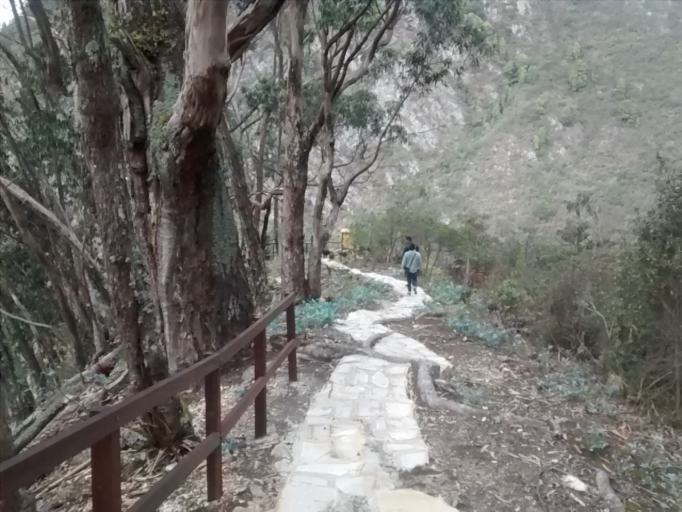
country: CO
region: Bogota D.C.
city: Bogota
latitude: 4.5984
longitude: -74.0584
